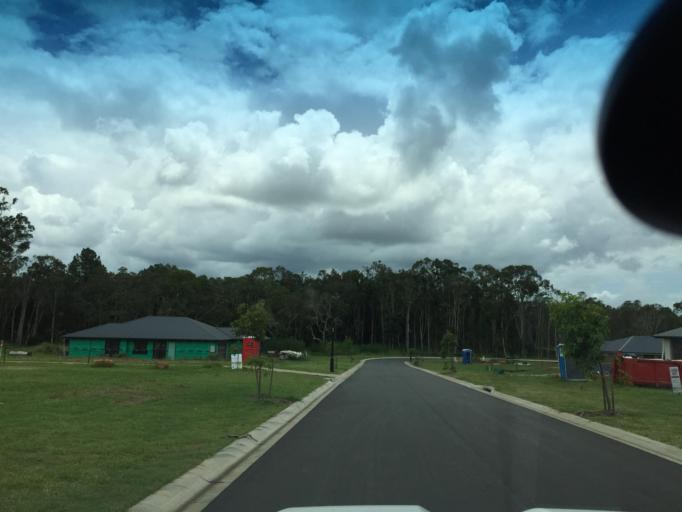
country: AU
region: Queensland
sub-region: Moreton Bay
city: Caboolture
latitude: -27.0413
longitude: 152.9201
